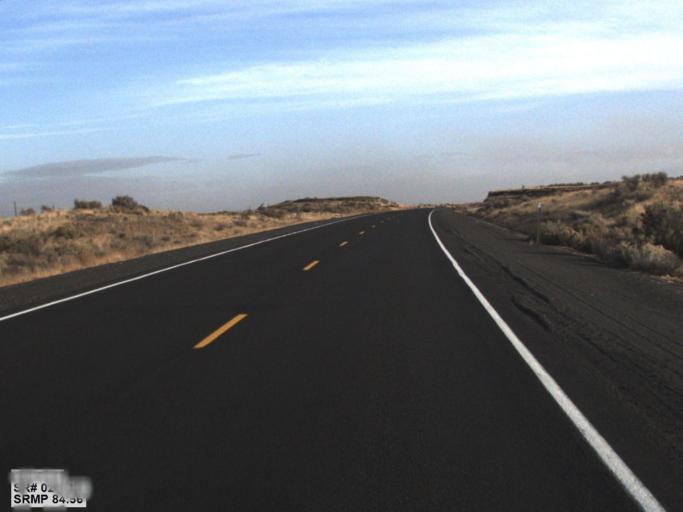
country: US
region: Washington
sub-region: Grant County
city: Warden
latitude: 47.3287
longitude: -118.8750
